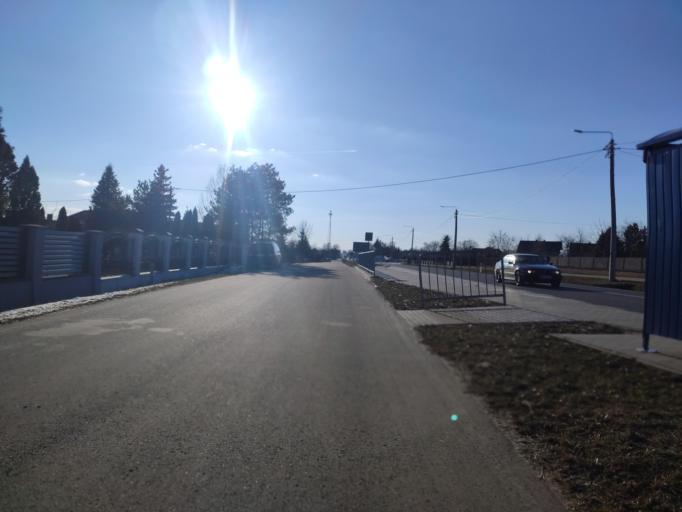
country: PL
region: Lublin Voivodeship
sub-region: Powiat lubartowski
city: Kock
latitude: 51.6435
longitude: 22.4349
